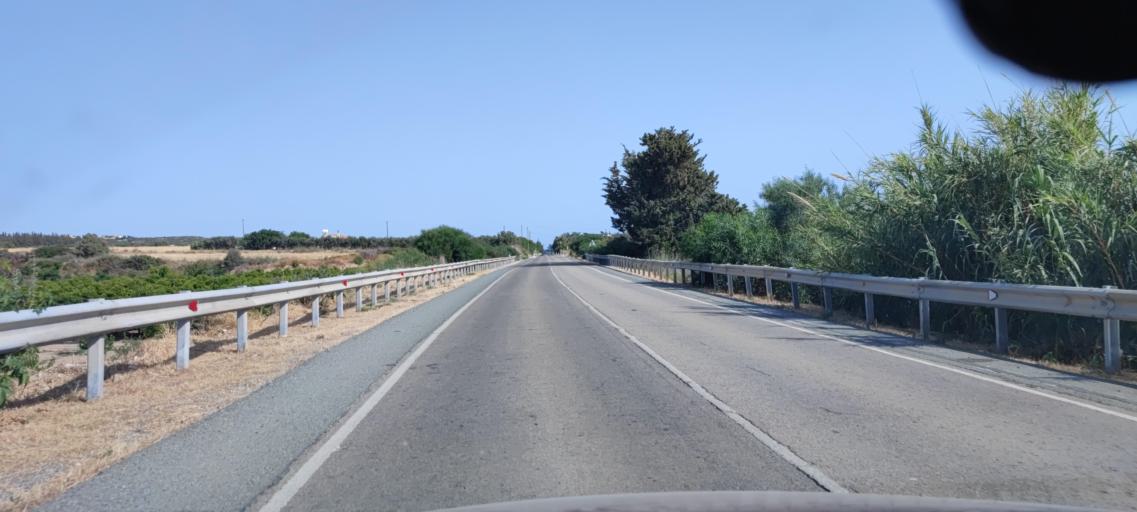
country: CY
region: Limassol
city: Pissouri
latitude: 34.7002
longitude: 32.5741
